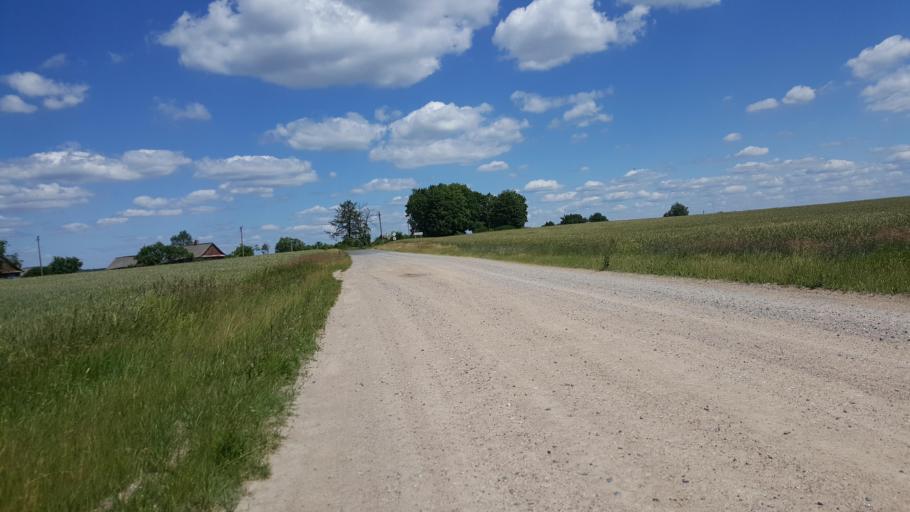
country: PL
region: Podlasie
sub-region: Powiat hajnowski
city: Czeremcha
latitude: 52.4981
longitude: 23.4690
